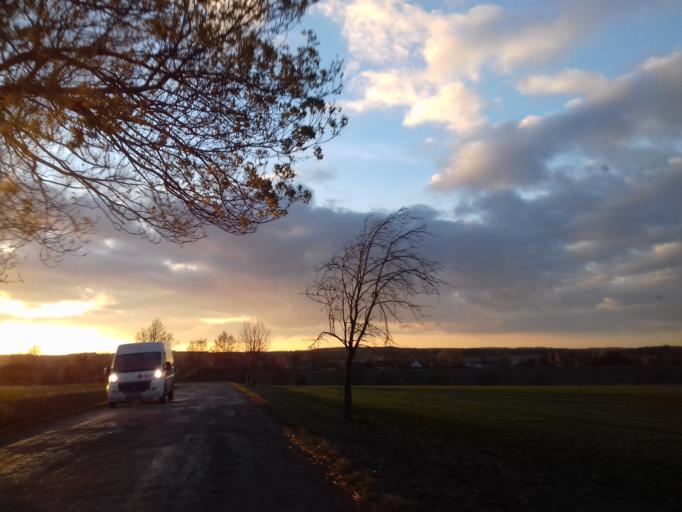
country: CZ
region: Pardubicky
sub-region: Okres Chrudim
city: Hlinsko
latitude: 49.7931
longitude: 15.9351
